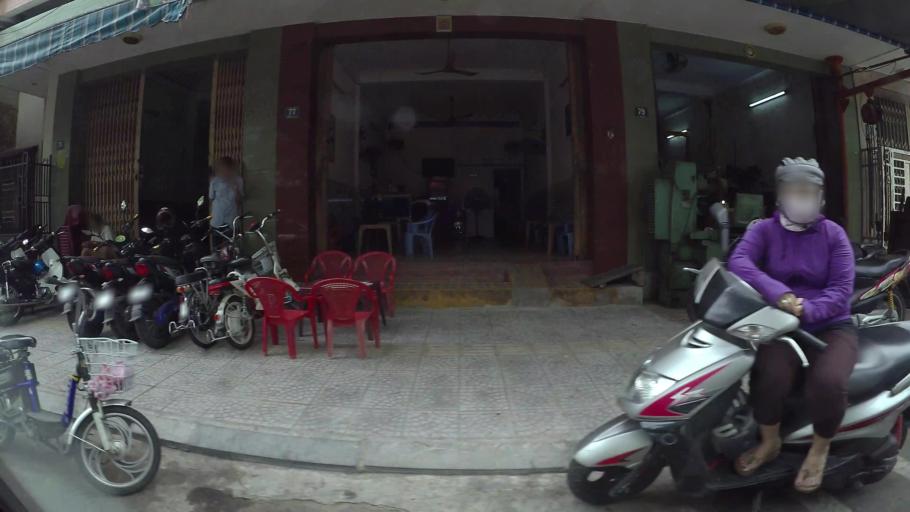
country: VN
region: Da Nang
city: Da Nang
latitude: 16.0588
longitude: 108.2123
